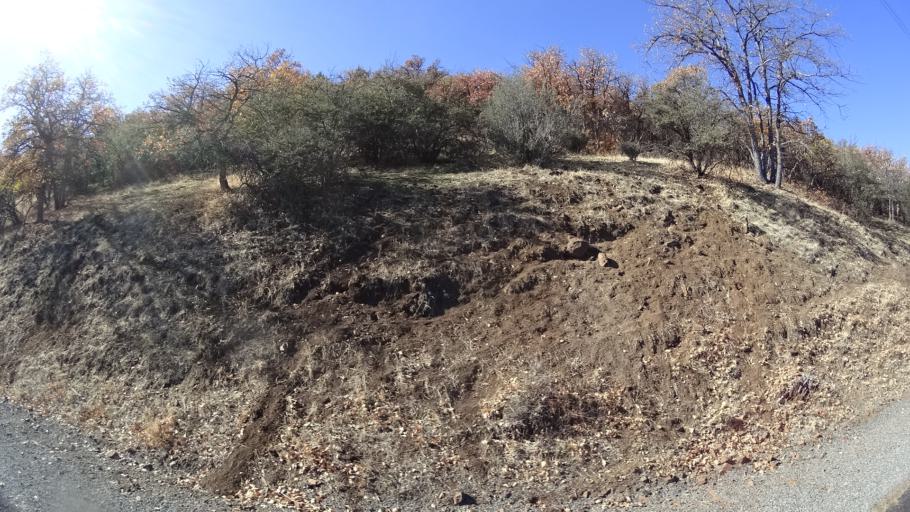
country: US
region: California
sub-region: Siskiyou County
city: Montague
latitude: 41.8778
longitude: -122.4924
